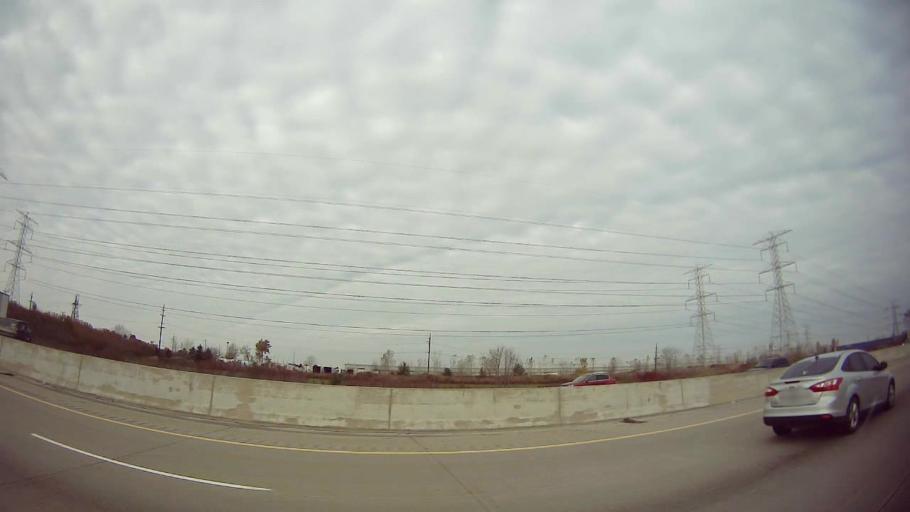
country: US
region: Michigan
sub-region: Wayne County
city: Woodhaven
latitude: 42.1095
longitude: -83.2414
